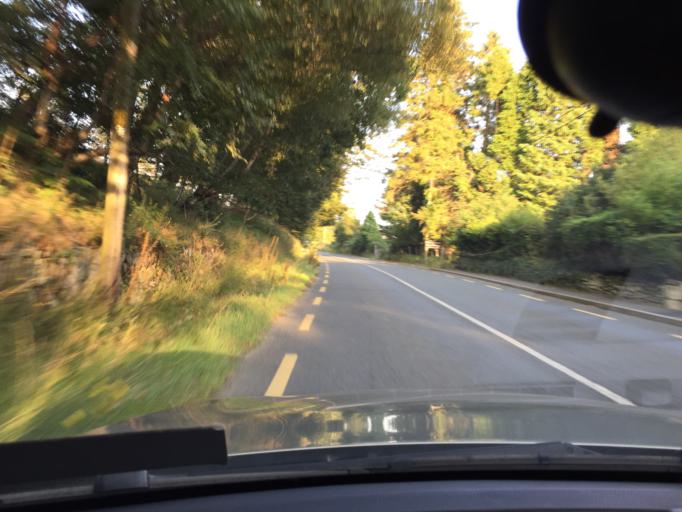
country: IE
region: Leinster
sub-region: Wicklow
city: Rathdrum
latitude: 53.0092
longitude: -6.3105
